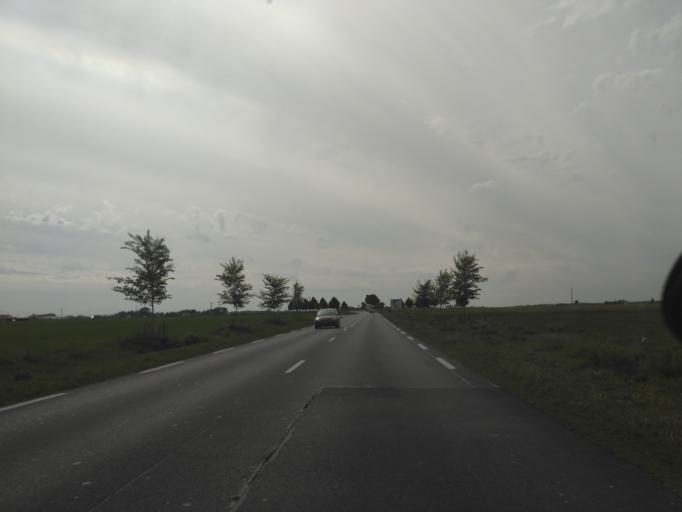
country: FR
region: Ile-de-France
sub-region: Departement de Seine-et-Marne
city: Soignolles-en-Brie
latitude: 48.6331
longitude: 2.7049
